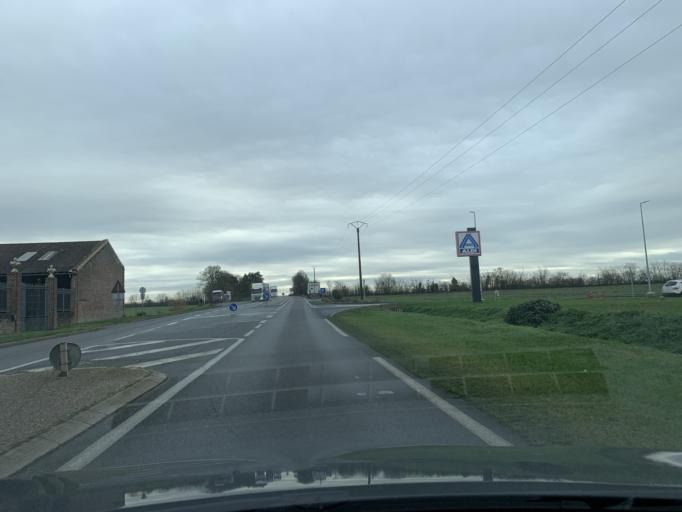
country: FR
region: Nord-Pas-de-Calais
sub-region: Departement du Nord
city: Aubigny-au-Bac
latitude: 50.2533
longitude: 3.1625
